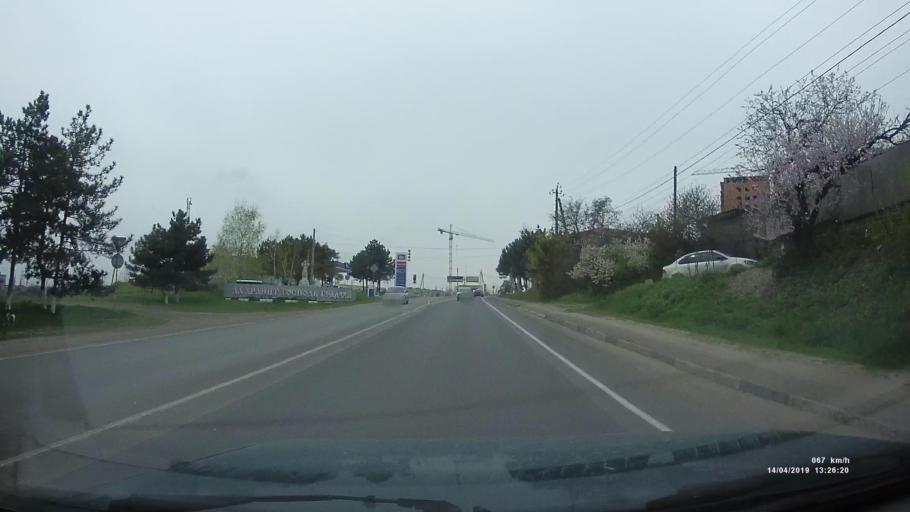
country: RU
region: Rostov
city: Azov
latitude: 47.0898
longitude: 39.4557
